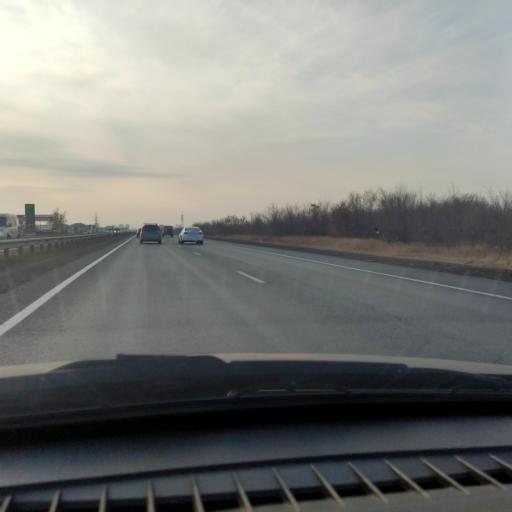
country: RU
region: Samara
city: Tol'yatti
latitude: 53.5662
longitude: 49.3733
